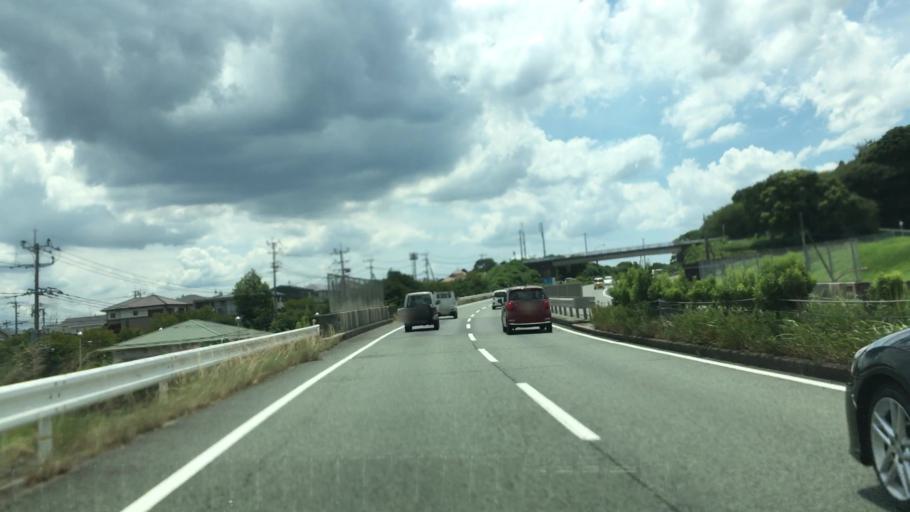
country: JP
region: Saga Prefecture
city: Tosu
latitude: 33.4035
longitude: 130.5135
